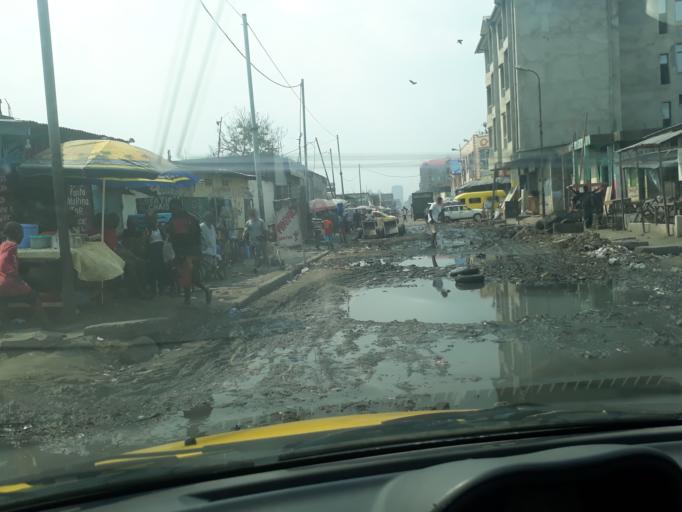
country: CD
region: Kinshasa
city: Kinshasa
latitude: -4.3247
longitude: 15.3169
